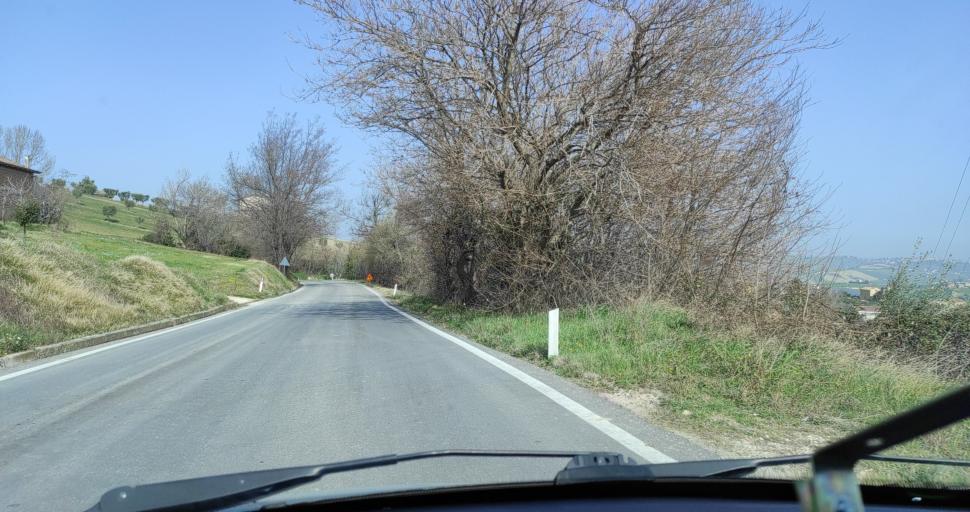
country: IT
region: The Marches
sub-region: Provincia di Macerata
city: Loro Piceno
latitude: 43.1680
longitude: 13.4253
